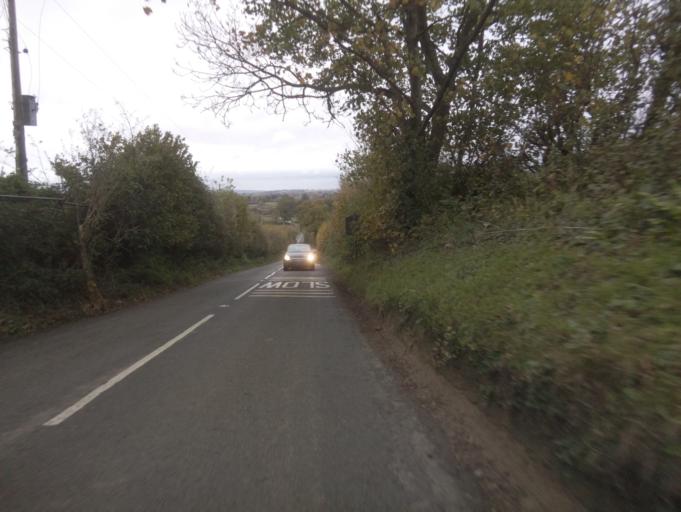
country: GB
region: England
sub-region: Dorset
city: Sherborne
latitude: 50.9840
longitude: -2.5676
